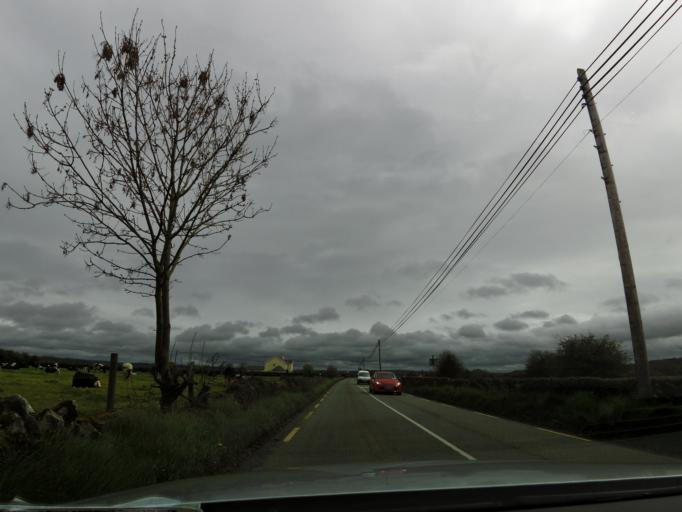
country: IE
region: Leinster
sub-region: Kilkenny
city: Ballyragget
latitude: 52.7362
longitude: -7.4213
